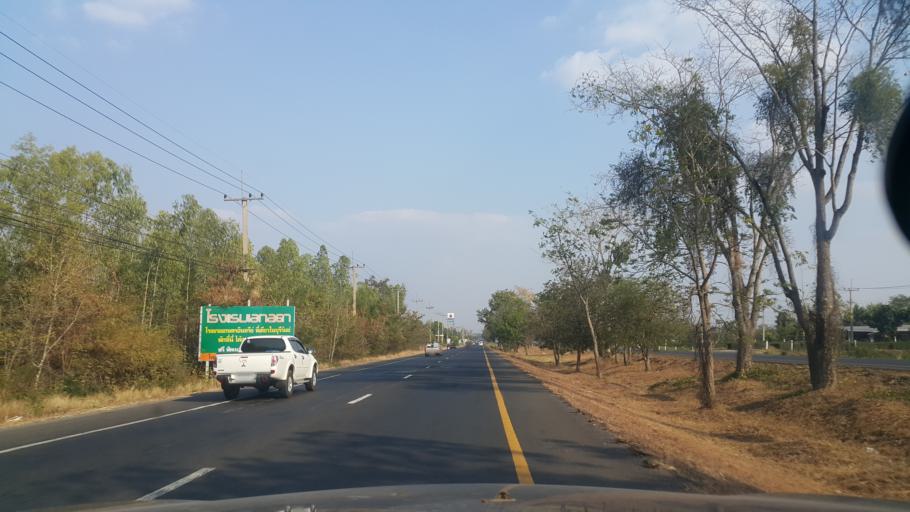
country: TH
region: Buriram
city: Nang Rong
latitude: 14.6394
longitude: 102.6971
